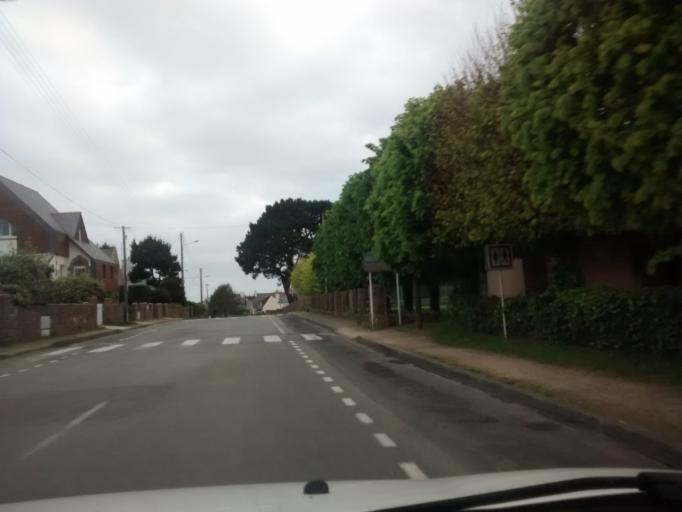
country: FR
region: Brittany
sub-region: Departement des Cotes-d'Armor
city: Tregastel
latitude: 48.8249
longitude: -3.4805
